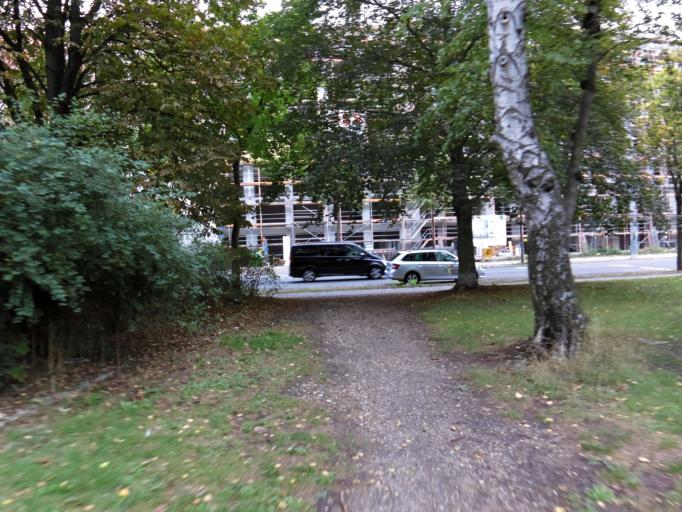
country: DE
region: Saxony
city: Leipzig
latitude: 51.3382
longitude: 12.3898
